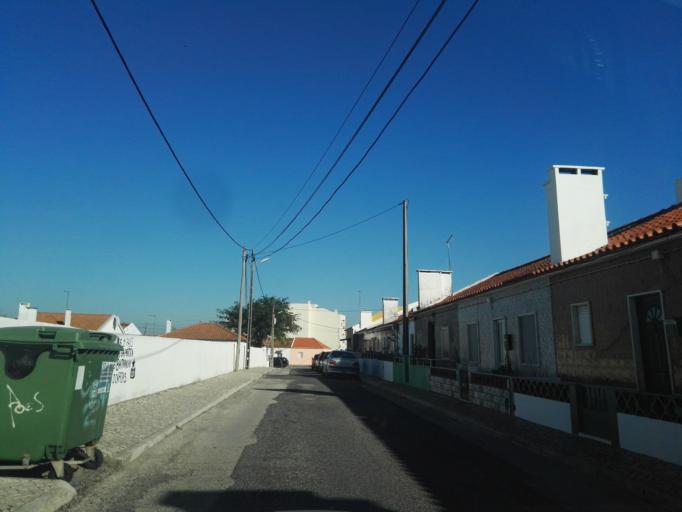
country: PT
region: Santarem
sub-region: Benavente
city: Samora Correia
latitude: 38.9349
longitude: -8.8768
